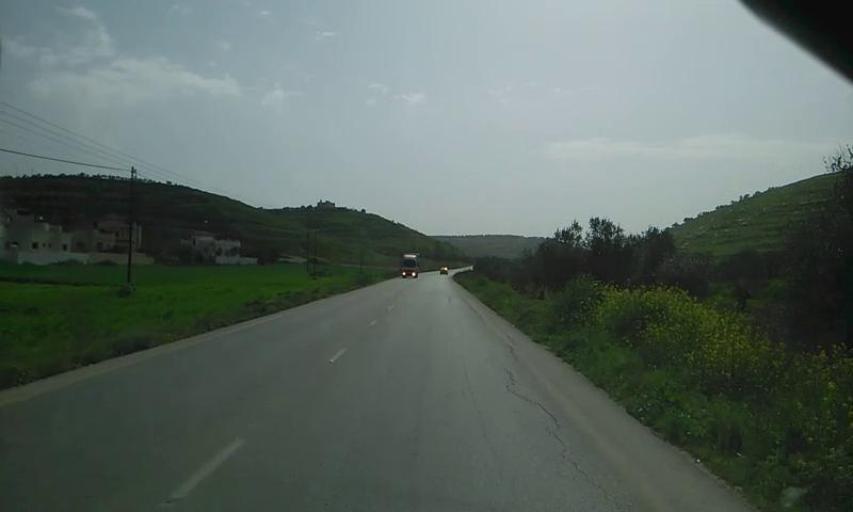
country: PS
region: West Bank
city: Mirkah
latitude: 32.3927
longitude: 35.2195
